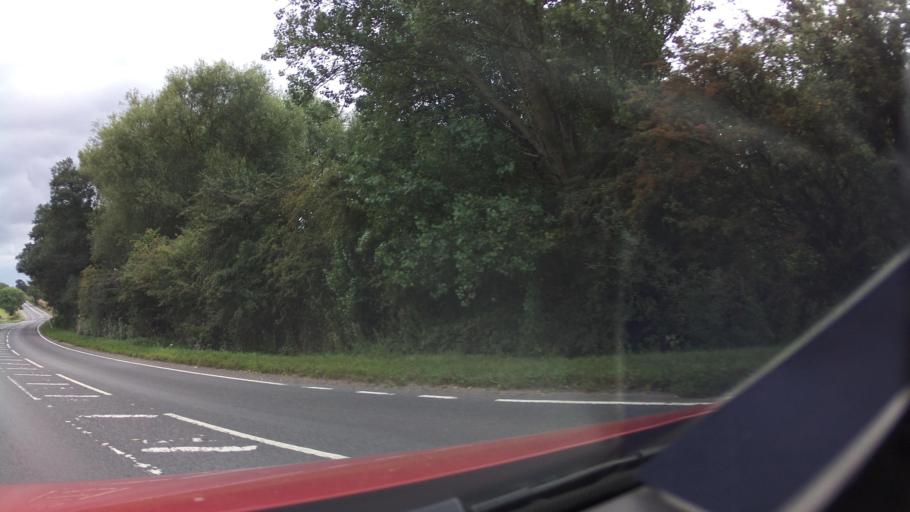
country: GB
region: England
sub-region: Warwickshire
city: Curdworth
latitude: 52.5717
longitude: -1.7642
